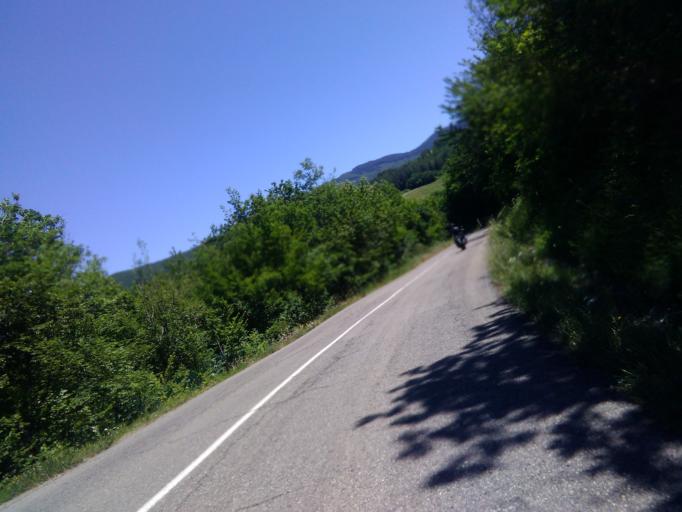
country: IT
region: Emilia-Romagna
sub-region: Provincia di Parma
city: Calestano
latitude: 44.5910
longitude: 10.1136
